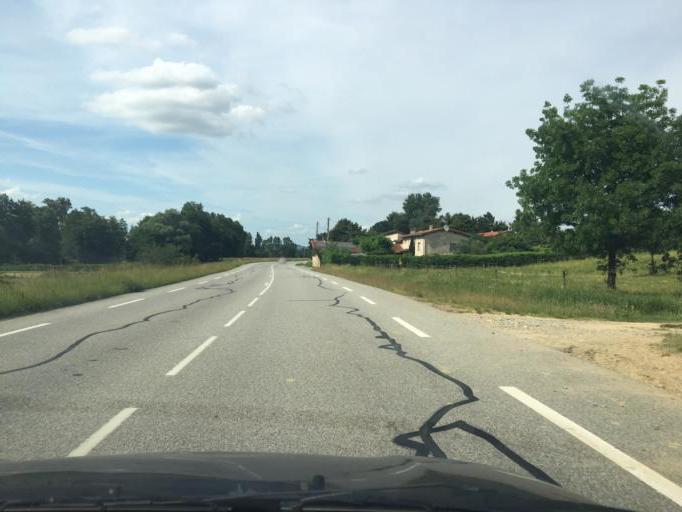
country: FR
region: Rhone-Alpes
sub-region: Departement de la Drome
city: Chanos-Curson
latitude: 45.0650
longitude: 4.9320
